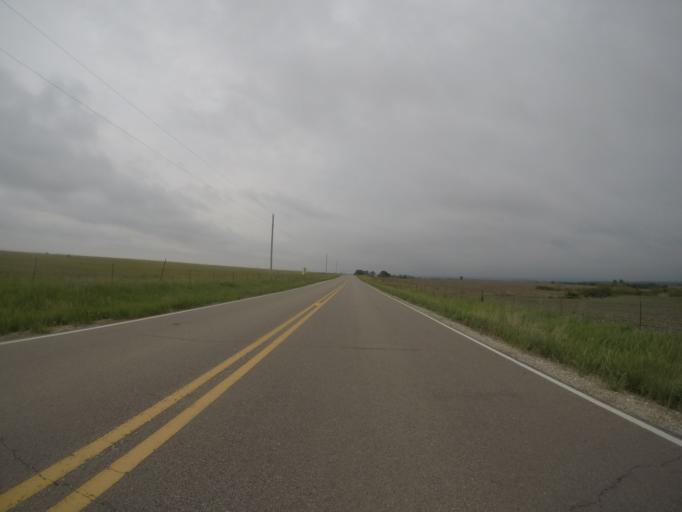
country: US
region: Kansas
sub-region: Pottawatomie County
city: Westmoreland
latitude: 39.5115
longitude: -96.2300
